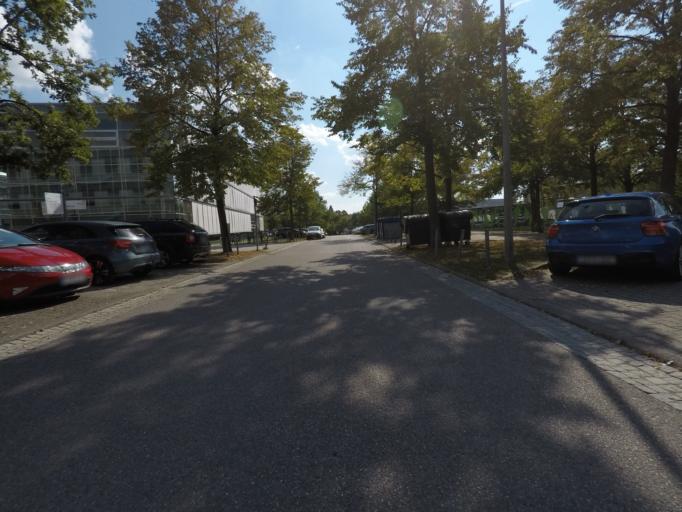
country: DE
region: Baden-Wuerttemberg
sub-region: Regierungsbezirk Stuttgart
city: Gerlingen
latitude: 48.7419
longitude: 9.0956
